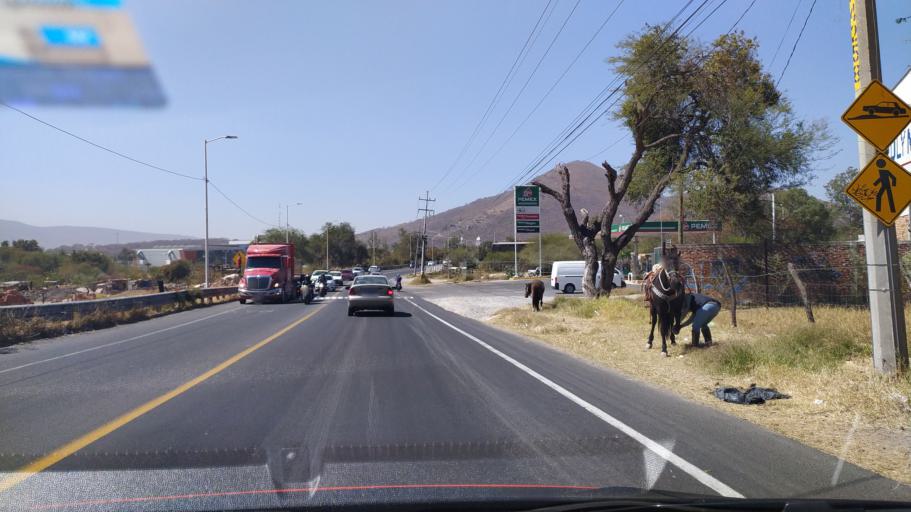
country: MX
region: Jalisco
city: Tlajomulco de Zuniga
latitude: 20.4777
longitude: -103.4382
